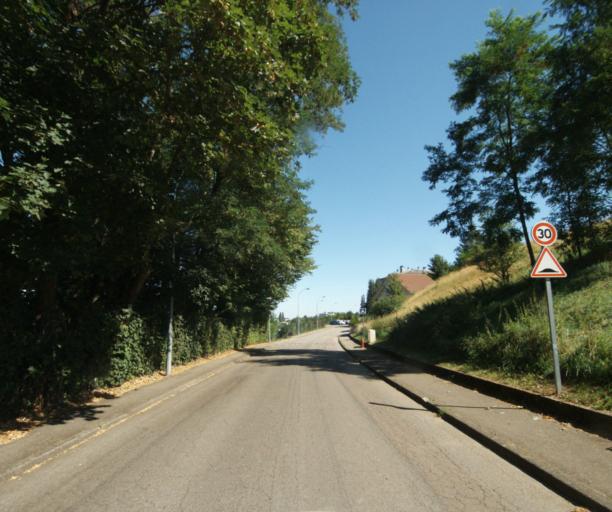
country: FR
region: Lorraine
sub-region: Departement des Vosges
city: Epinal
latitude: 48.1810
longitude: 6.4511
